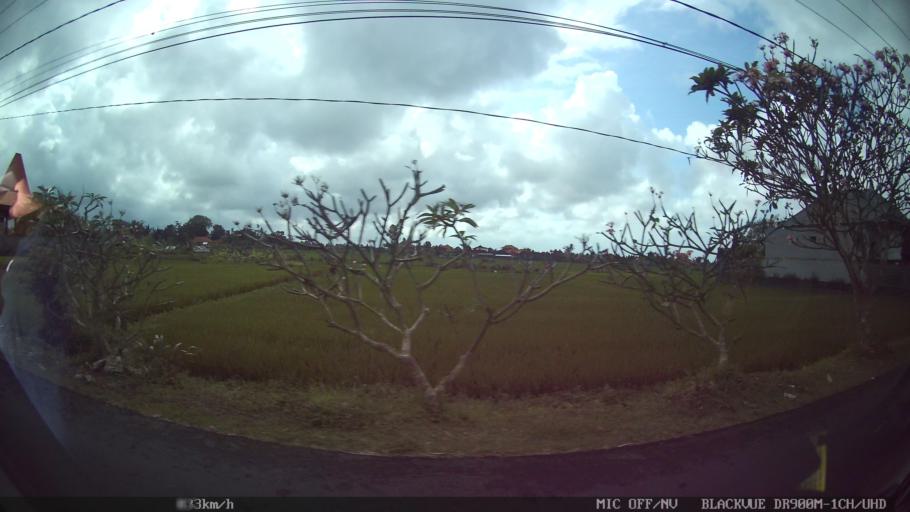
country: ID
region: Bali
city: Banjar Bucu
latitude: -8.5942
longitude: 115.2063
